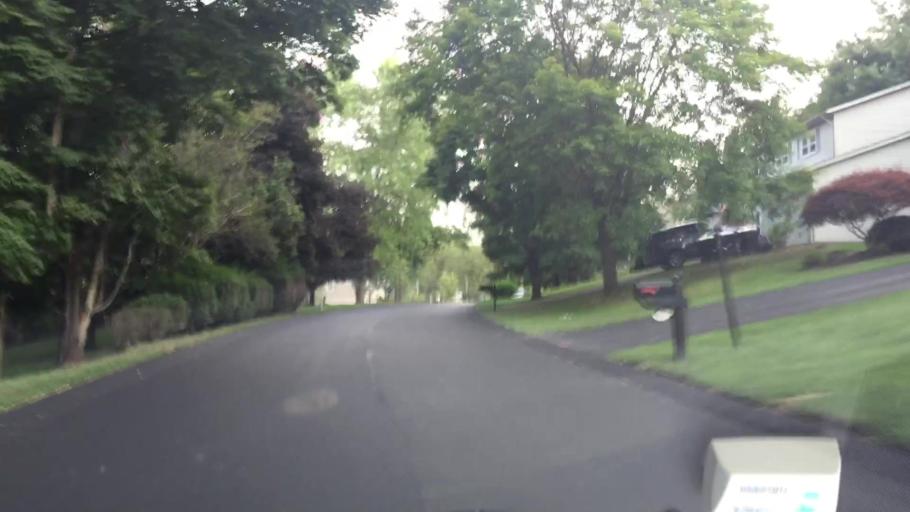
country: US
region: Pennsylvania
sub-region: Allegheny County
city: Franklin Park
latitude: 40.5763
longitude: -80.0508
